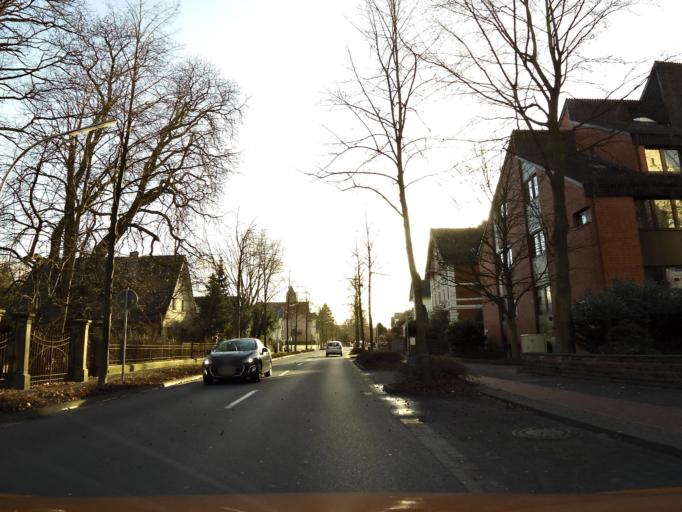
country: DE
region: Lower Saxony
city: Verden
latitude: 52.9181
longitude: 9.2322
